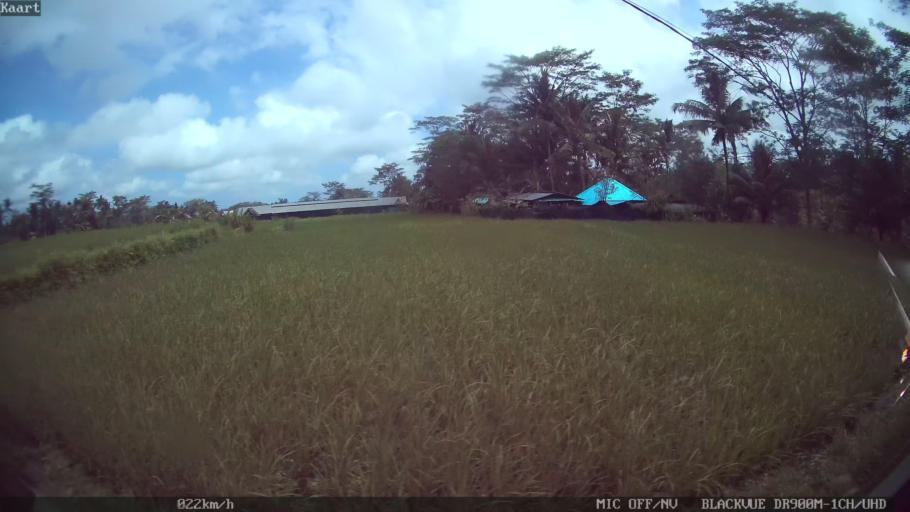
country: ID
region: Bali
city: Banjar Susut Kaja
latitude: -8.4457
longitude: 115.3285
